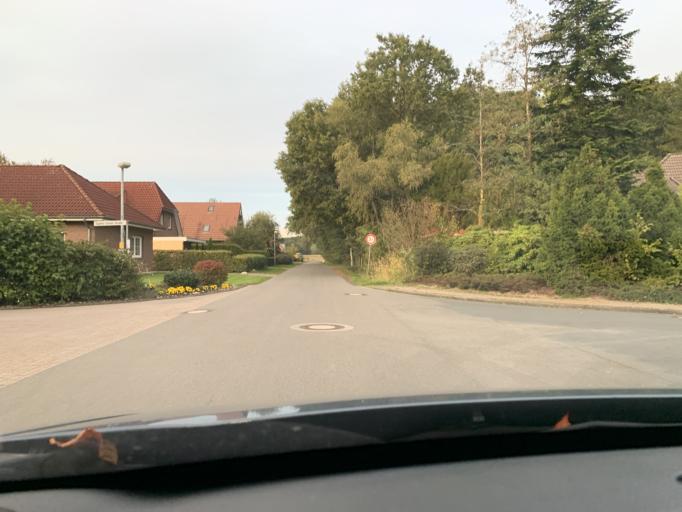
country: DE
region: Lower Saxony
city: Westerstede
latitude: 53.2560
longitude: 7.9042
